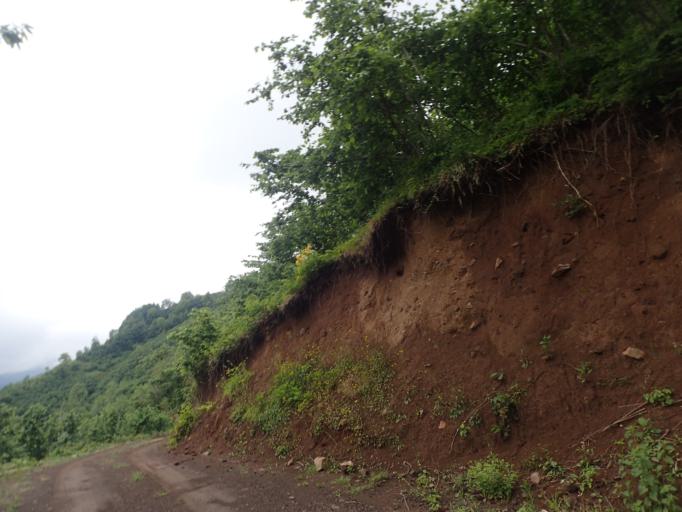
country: TR
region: Samsun
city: Salipazari
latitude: 40.9424
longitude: 36.8931
